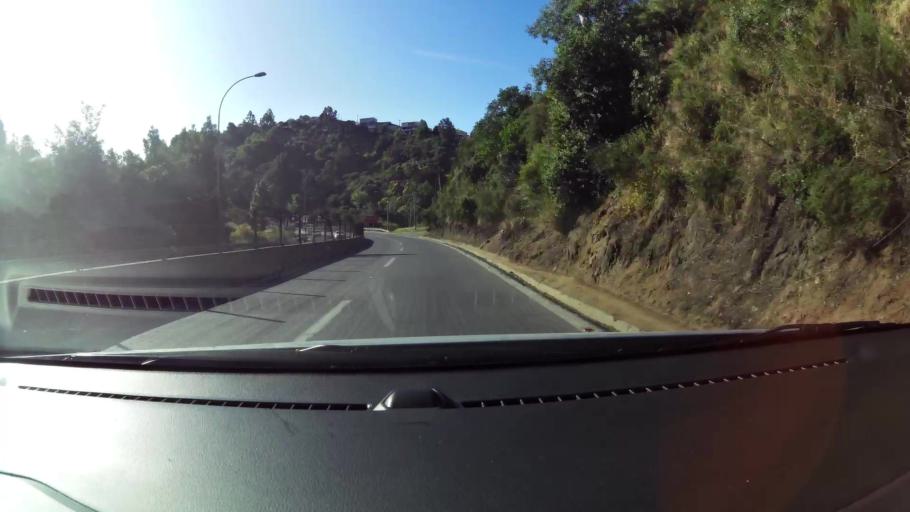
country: CL
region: Valparaiso
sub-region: Provincia de Valparaiso
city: Valparaiso
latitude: -33.0510
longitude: -71.5887
